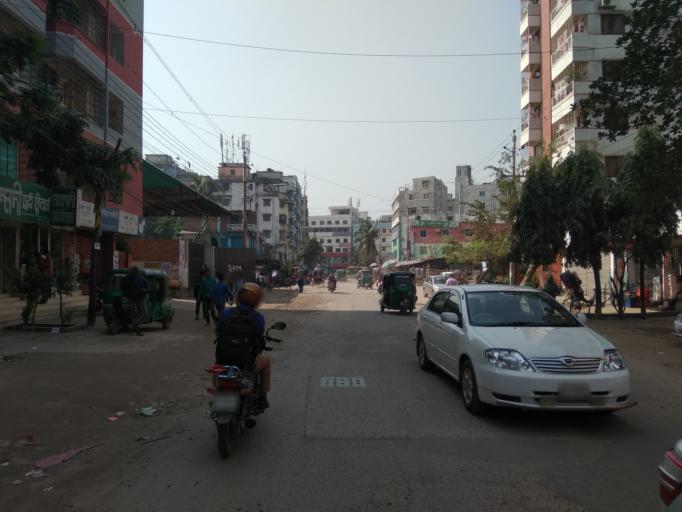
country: BD
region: Dhaka
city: Tungi
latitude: 23.8172
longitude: 90.3575
